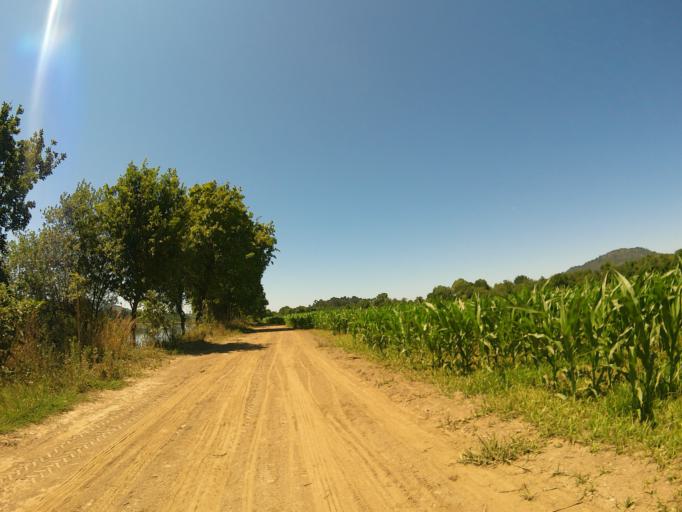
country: PT
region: Viana do Castelo
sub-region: Viana do Castelo
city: Darque
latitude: 41.7152
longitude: -8.7093
